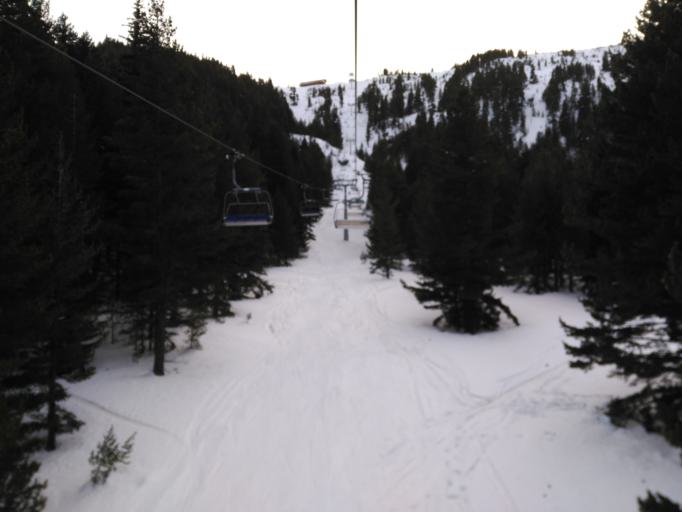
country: BG
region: Blagoevgrad
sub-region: Obshtina Bansko
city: Bansko
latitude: 41.7681
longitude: 23.4483
